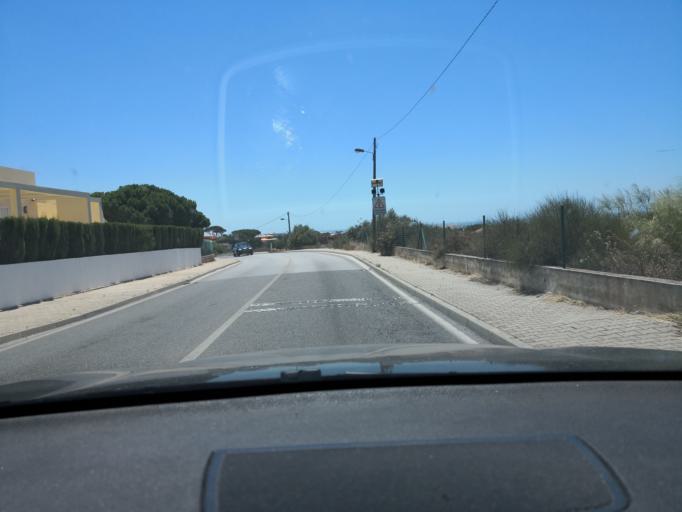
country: PT
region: Faro
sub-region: Albufeira
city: Ferreiras
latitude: 37.1065
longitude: -8.1999
